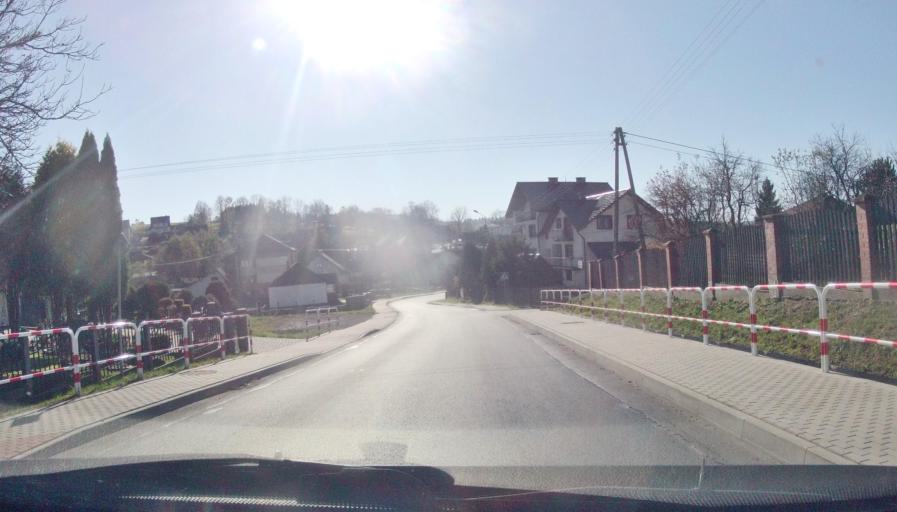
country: PL
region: Lesser Poland Voivodeship
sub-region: Powiat suski
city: Krzeszow
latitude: 49.7605
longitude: 19.4895
